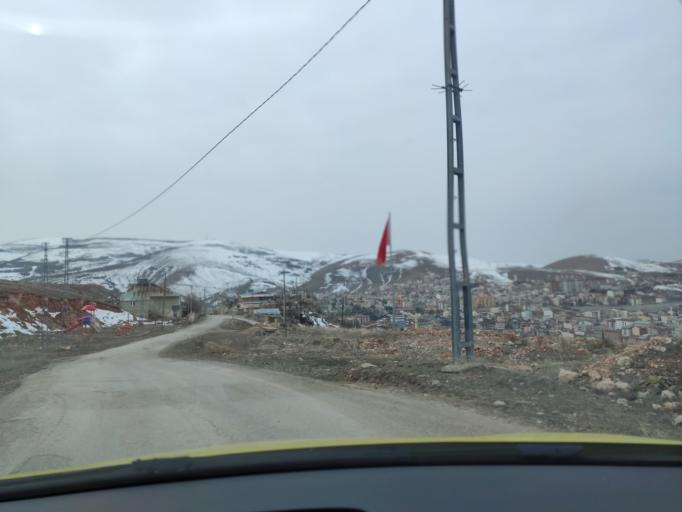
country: TR
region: Bayburt
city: Bayburt
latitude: 40.2588
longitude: 40.2344
